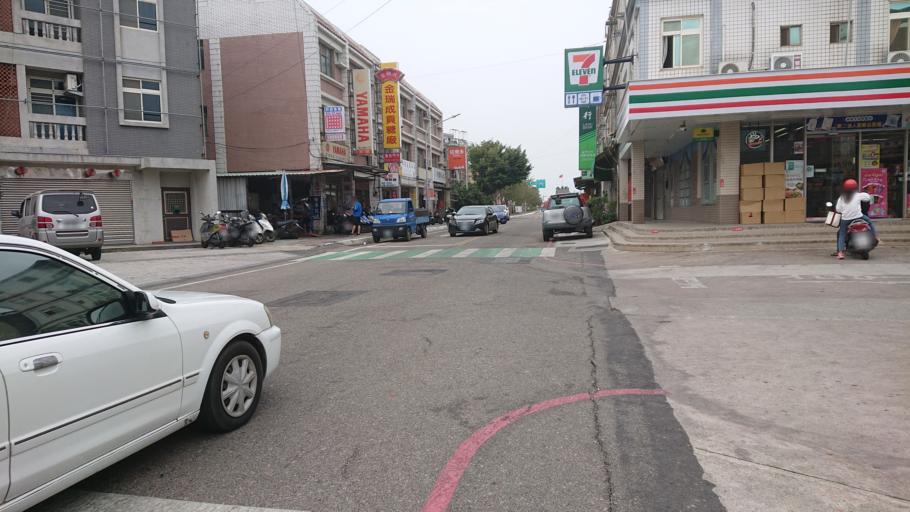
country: TW
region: Fukien
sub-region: Kinmen
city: Jincheng
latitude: 24.4285
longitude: 118.2475
